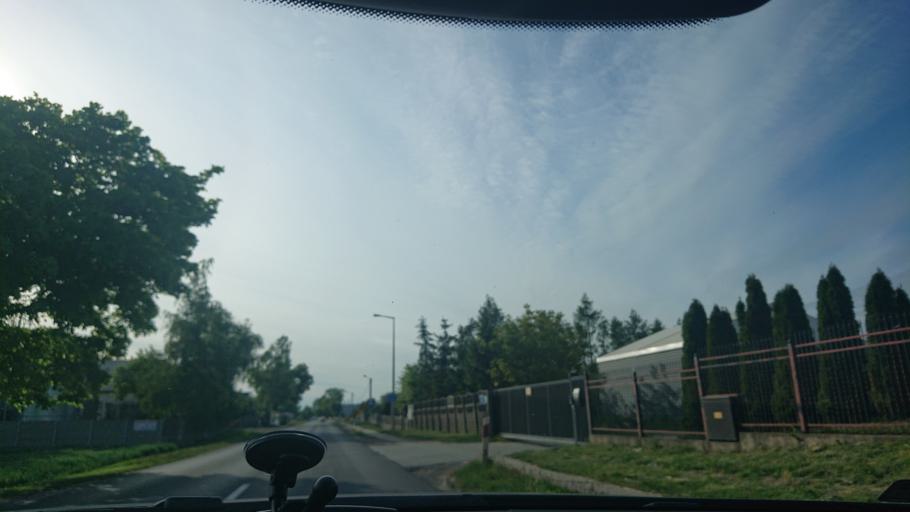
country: PL
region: Greater Poland Voivodeship
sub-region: Powiat gnieznienski
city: Gniezno
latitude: 52.5479
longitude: 17.5599
